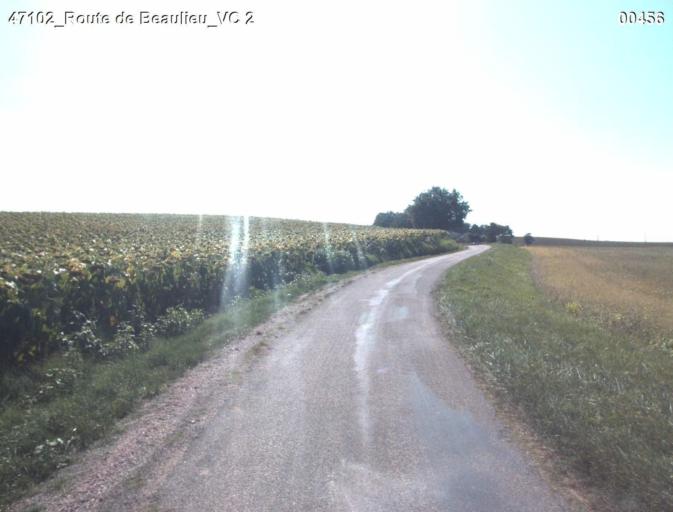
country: FR
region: Aquitaine
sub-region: Departement du Lot-et-Garonne
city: Laplume
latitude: 44.0827
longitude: 0.4437
